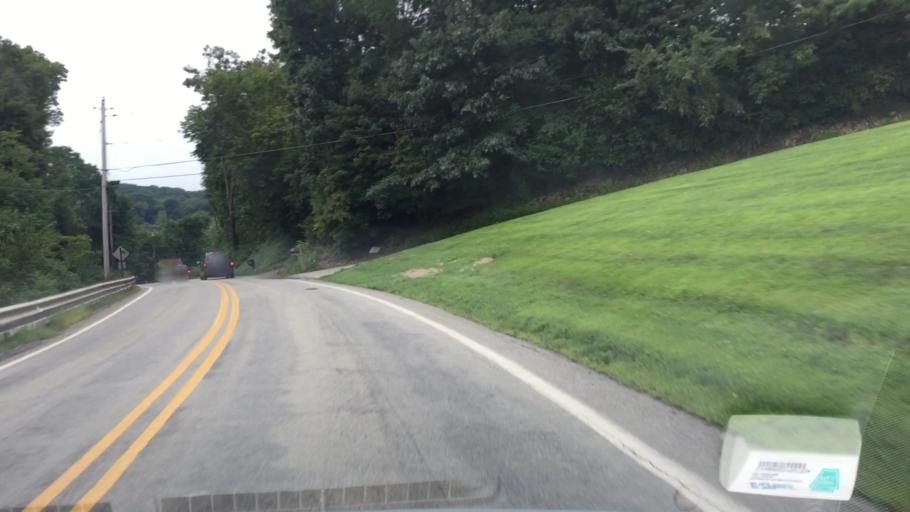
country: US
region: Pennsylvania
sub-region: Allegheny County
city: Curtisville
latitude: 40.6445
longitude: -79.8503
